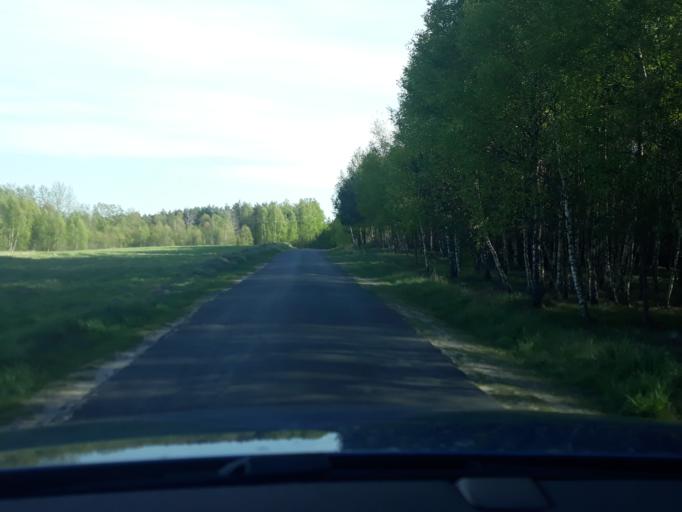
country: PL
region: Pomeranian Voivodeship
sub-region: Powiat czluchowski
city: Przechlewo
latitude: 53.8690
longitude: 17.3335
